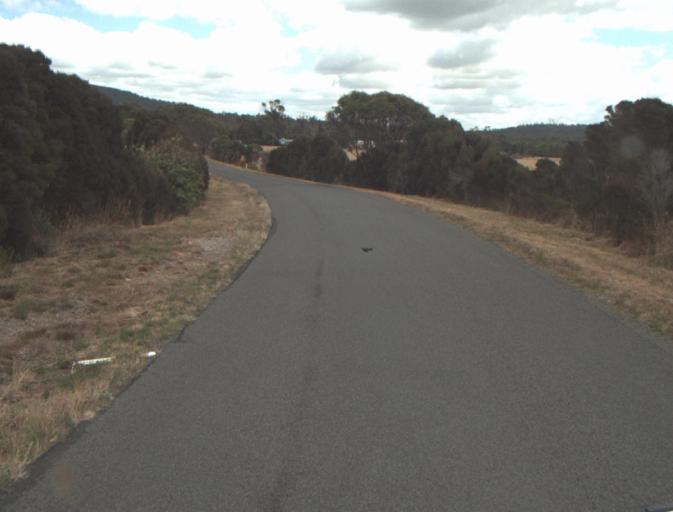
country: AU
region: Tasmania
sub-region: Launceston
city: Mayfield
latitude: -41.2064
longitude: 147.0619
